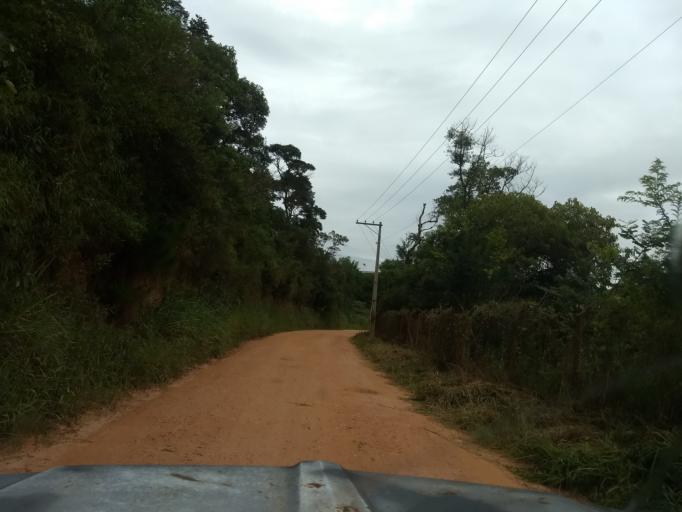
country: BR
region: Sao Paulo
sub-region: Cabreuva
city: Cabreuva
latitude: -23.4143
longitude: -47.1970
